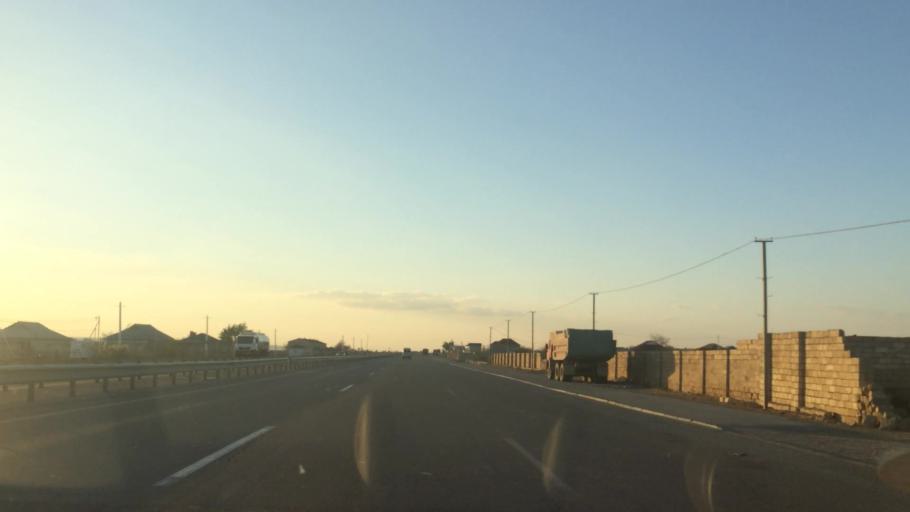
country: AZ
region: Baki
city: Qobustan
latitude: 39.9708
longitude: 49.2620
